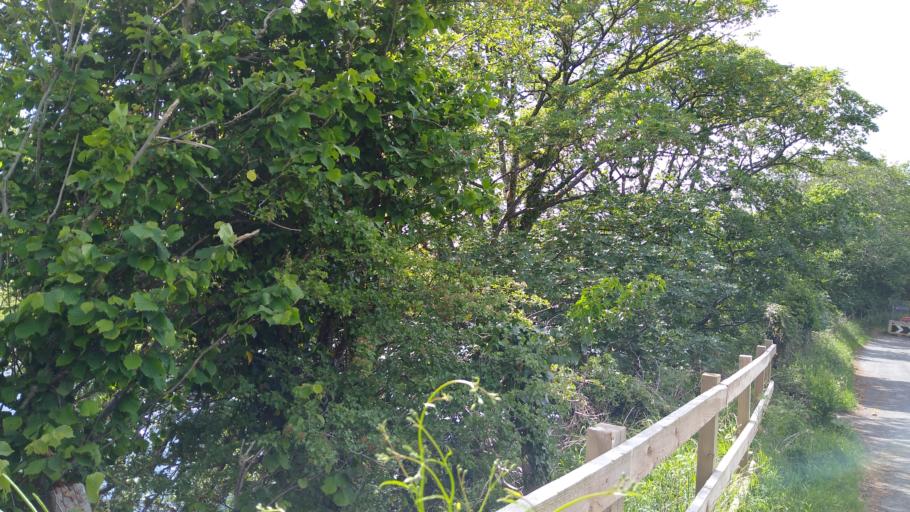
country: GB
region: England
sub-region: Cumbria
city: Flimby
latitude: 54.6628
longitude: -3.4826
